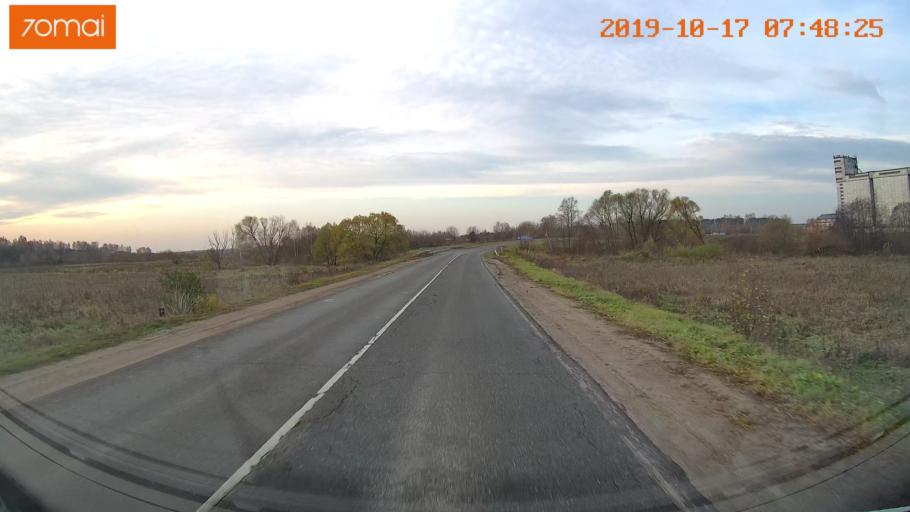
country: RU
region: Vladimir
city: Yur'yev-Pol'skiy
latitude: 56.4799
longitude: 39.6756
